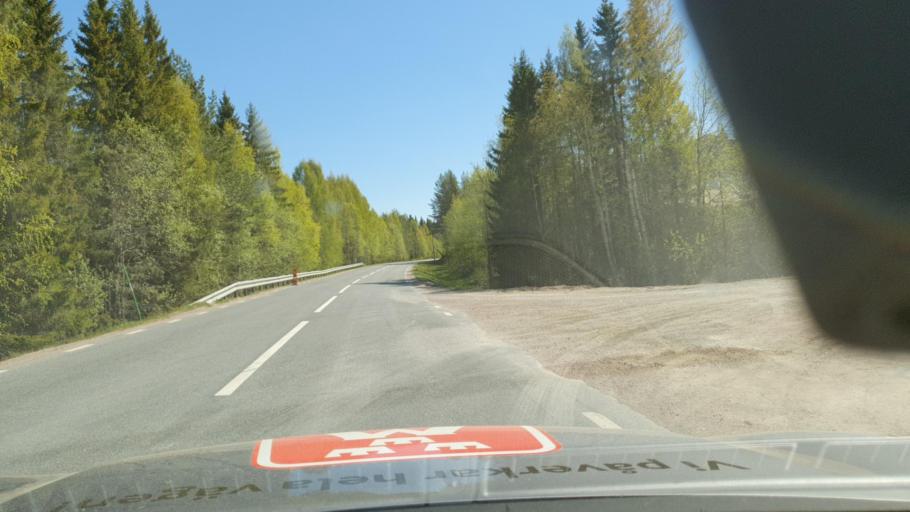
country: SE
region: Vaesternorrland
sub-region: OErnskoeldsviks Kommun
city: Ornskoldsvik
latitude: 63.6670
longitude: 18.5380
